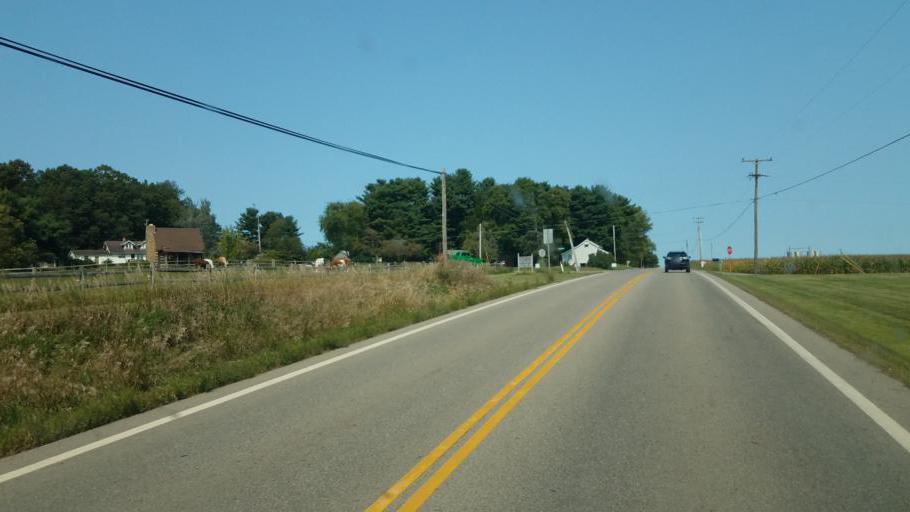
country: US
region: Ohio
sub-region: Wayne County
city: Shreve
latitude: 40.7403
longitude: -82.0247
